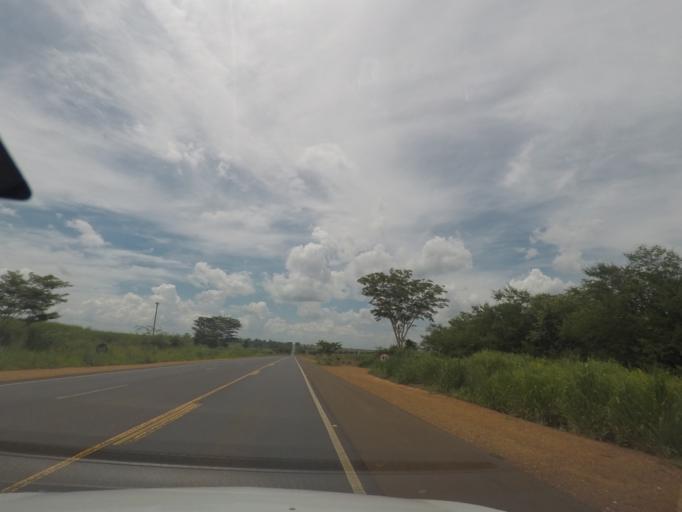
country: BR
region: Sao Paulo
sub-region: Barretos
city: Barretos
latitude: -20.4130
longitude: -48.6329
